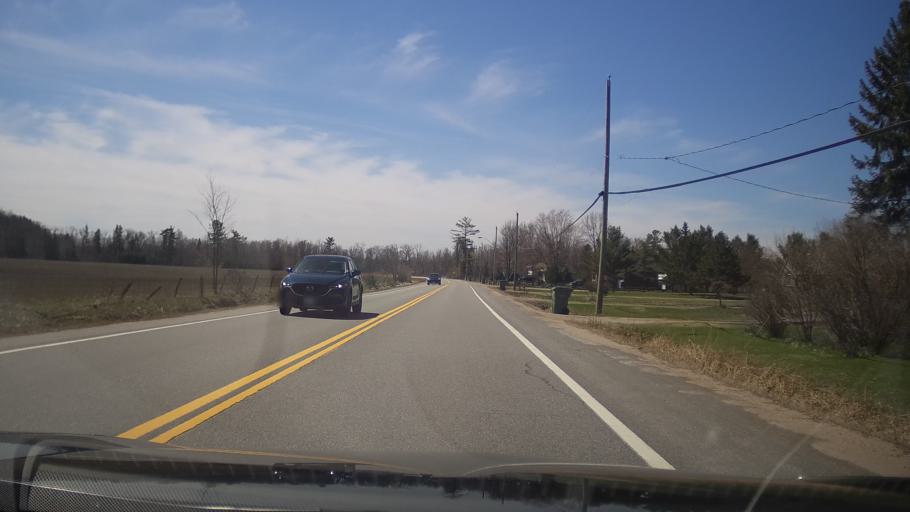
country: CA
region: Ontario
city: Bells Corners
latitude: 45.4841
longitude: -75.9526
